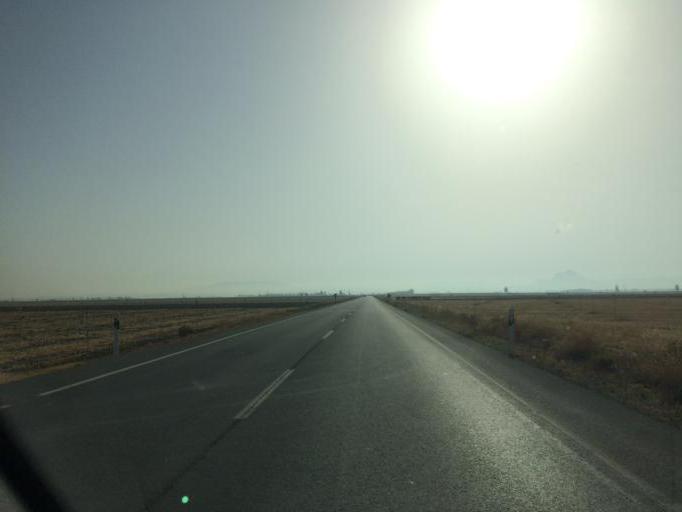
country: ES
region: Andalusia
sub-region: Provincia de Malaga
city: Mollina
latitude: 37.0592
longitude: -4.6244
